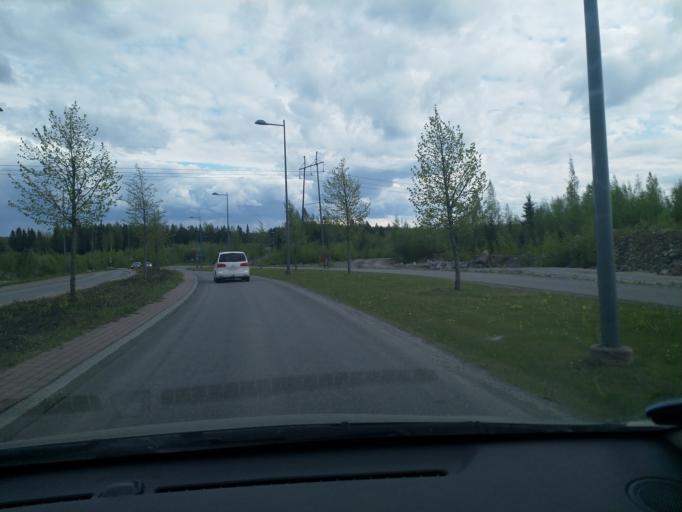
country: FI
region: Pirkanmaa
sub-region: Tampere
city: Tampere
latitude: 61.4578
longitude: 23.7913
